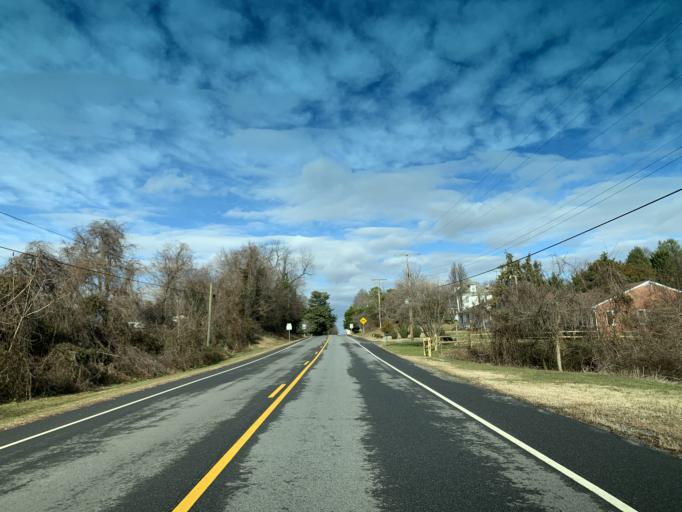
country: US
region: Maryland
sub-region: Harford County
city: Aberdeen Proving Ground
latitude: 39.3608
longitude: -76.0624
